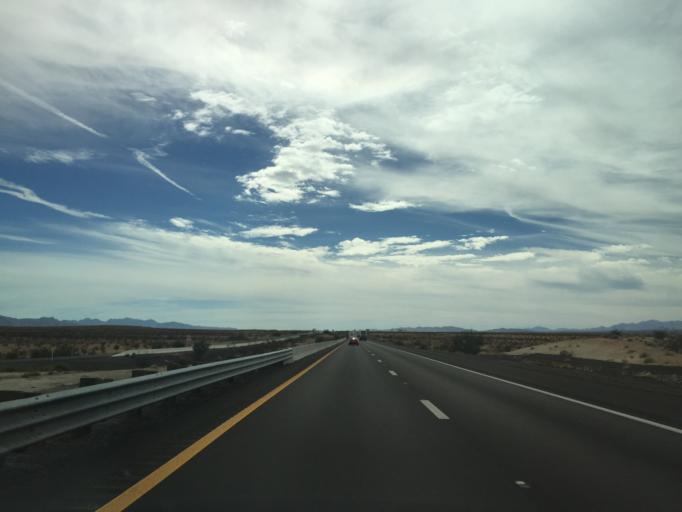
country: US
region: Nevada
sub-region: Clark County
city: Moapa Town
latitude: 36.5966
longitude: -114.6432
